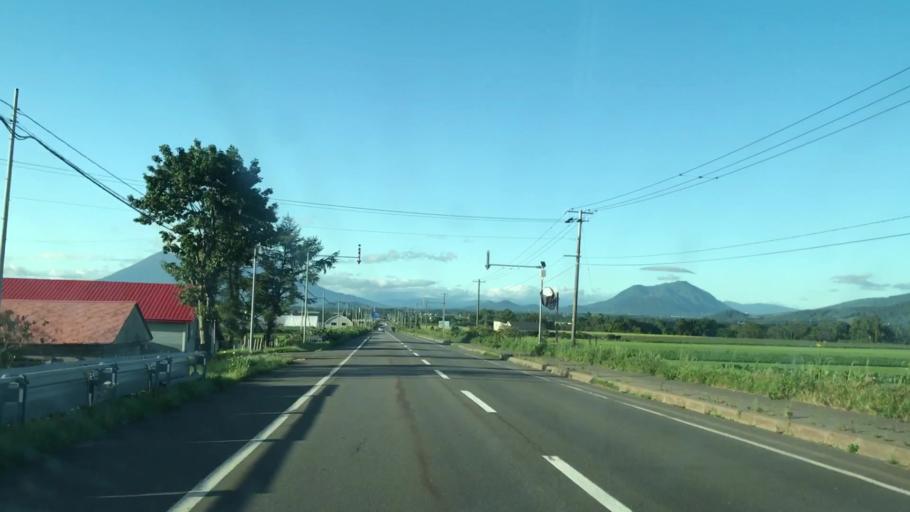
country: JP
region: Hokkaido
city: Date
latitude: 42.6367
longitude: 140.8018
